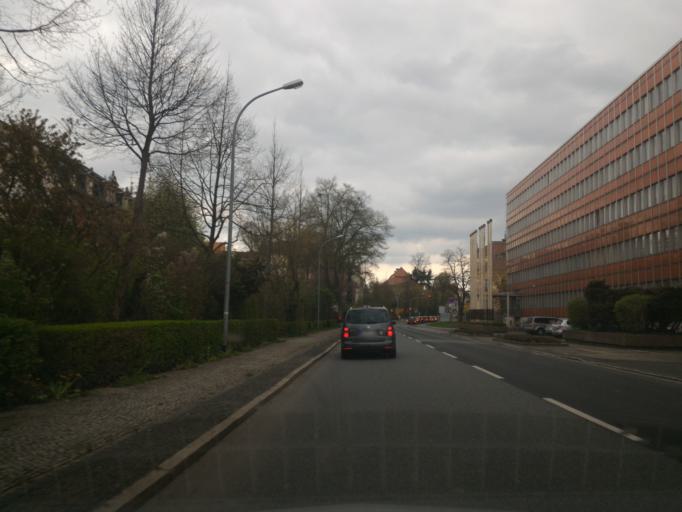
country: DE
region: Saxony
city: Zittau
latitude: 50.8936
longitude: 14.8054
